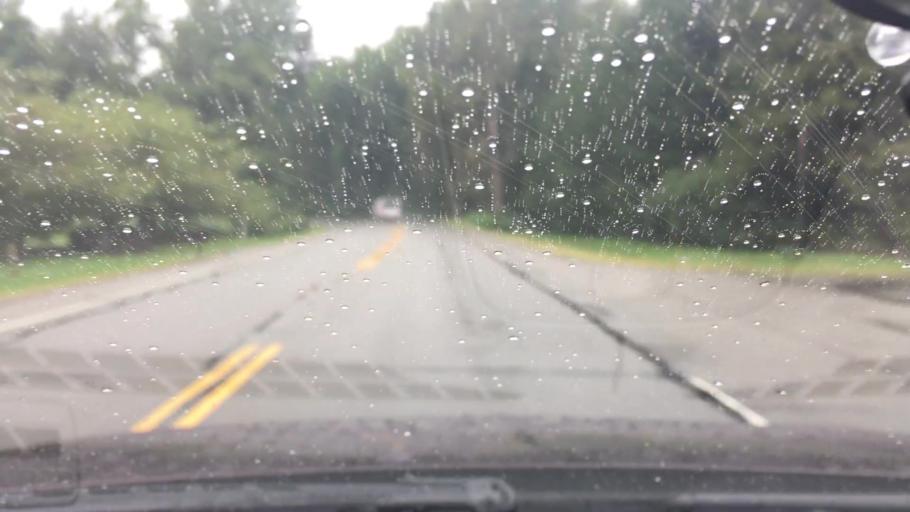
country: US
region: New York
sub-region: Dutchess County
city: Hillside Lake
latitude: 41.5723
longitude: -73.8216
